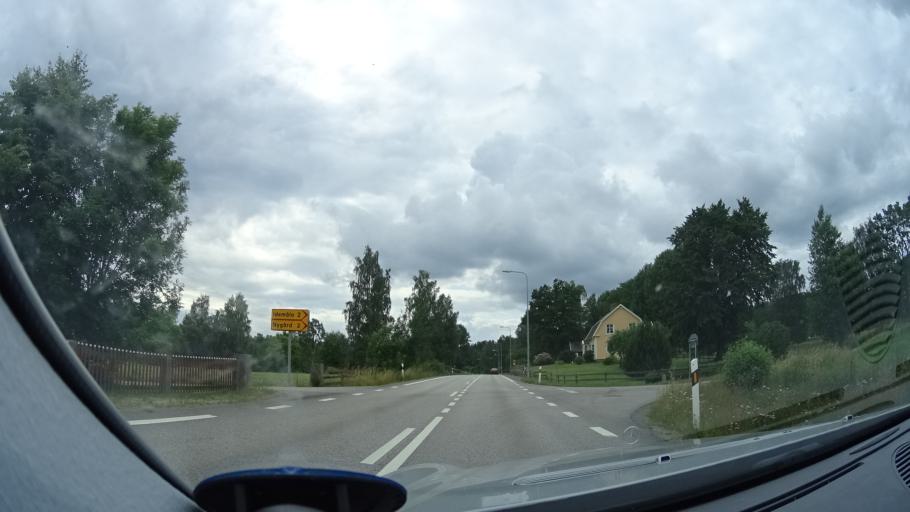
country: SE
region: Kronoberg
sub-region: Tingsryds Kommun
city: Tingsryd
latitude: 56.5002
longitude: 15.0503
